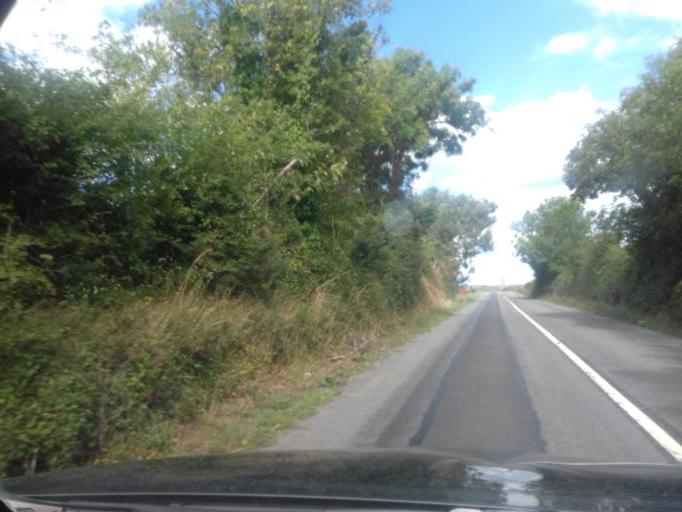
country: IE
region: Munster
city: Carrick-on-Suir
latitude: 52.2897
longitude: -7.4588
